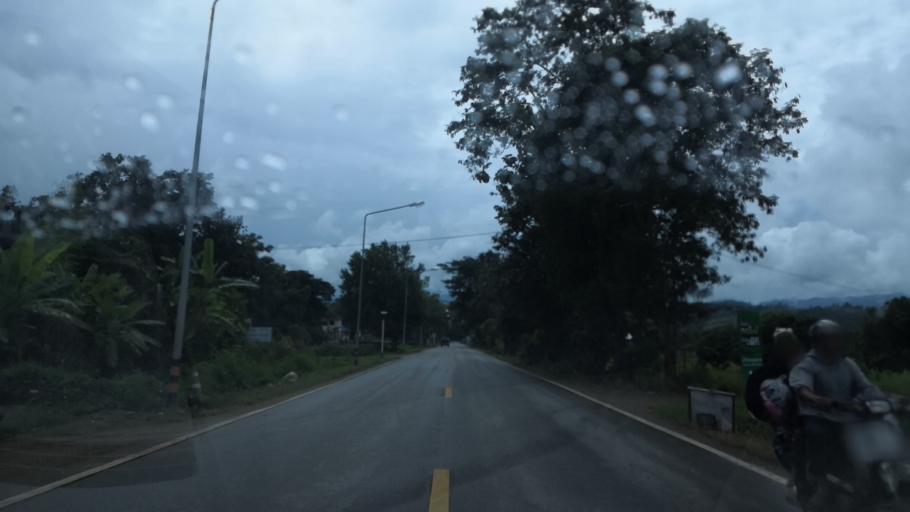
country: TH
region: Mae Hong Son
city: Mae La Noi
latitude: 18.3365
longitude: 97.9178
